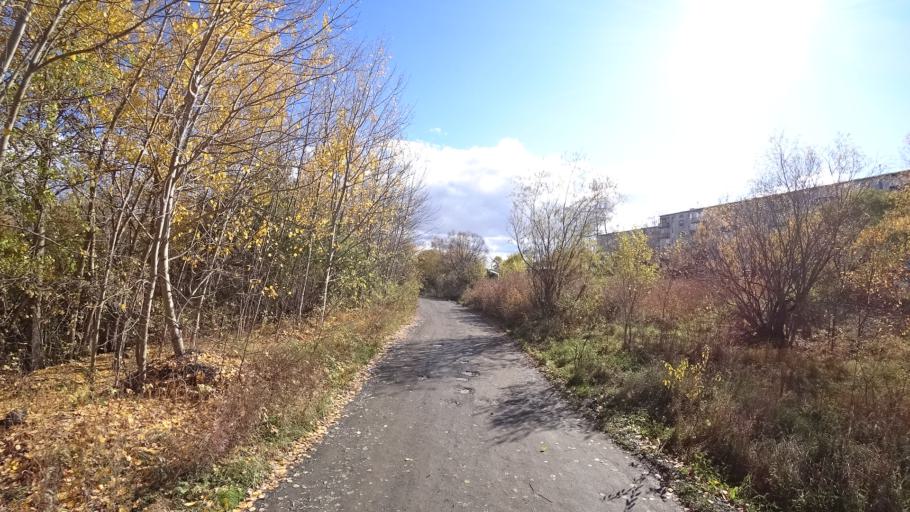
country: RU
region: Khabarovsk Krai
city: Amursk
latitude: 50.2227
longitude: 136.9095
